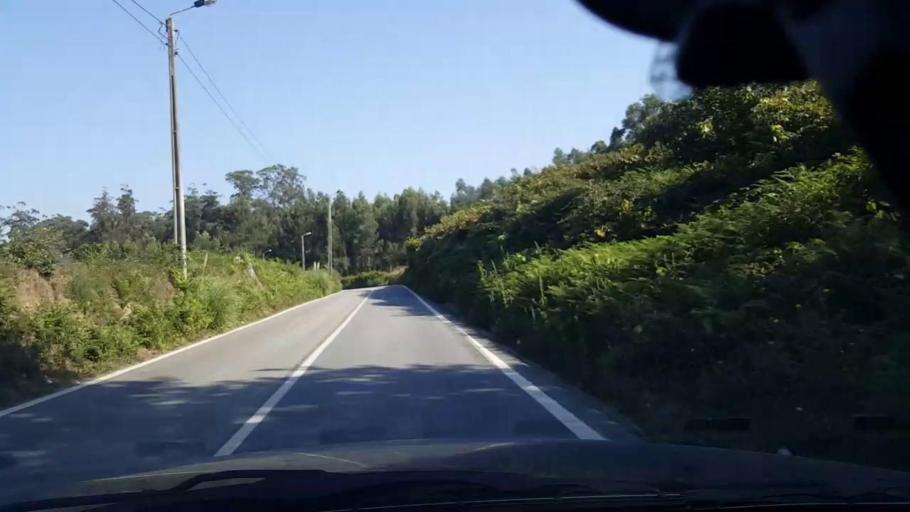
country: PT
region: Porto
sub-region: Maia
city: Gemunde
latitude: 41.2908
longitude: -8.6830
